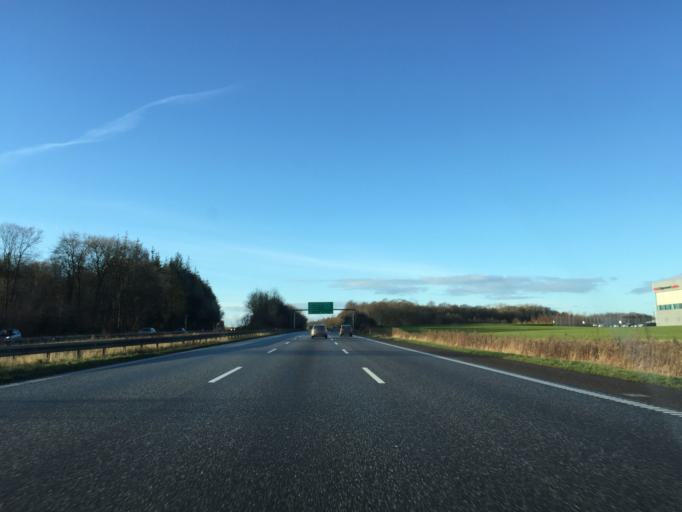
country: DK
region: South Denmark
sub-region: Fredericia Kommune
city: Snoghoj
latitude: 55.5391
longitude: 9.6766
